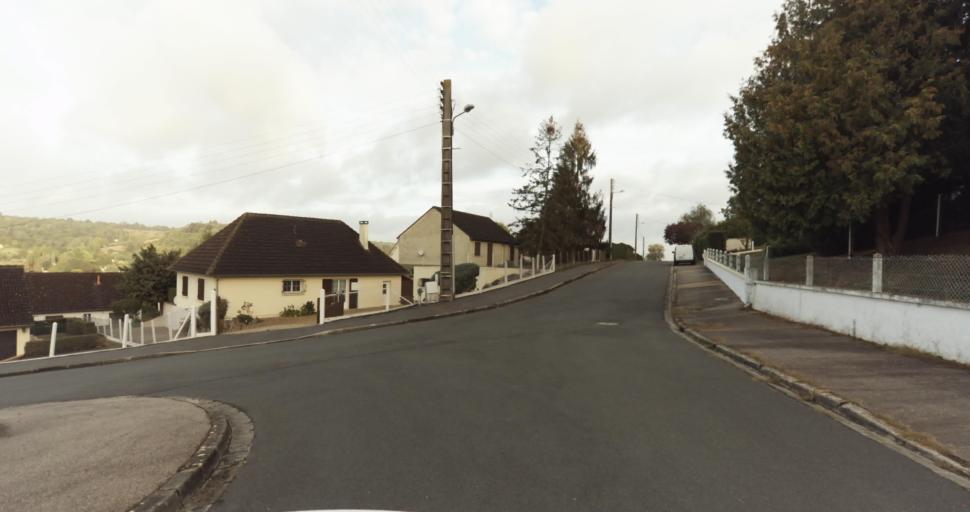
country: FR
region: Lower Normandy
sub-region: Departement de l'Orne
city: Vimoutiers
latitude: 48.9267
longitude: 0.2058
